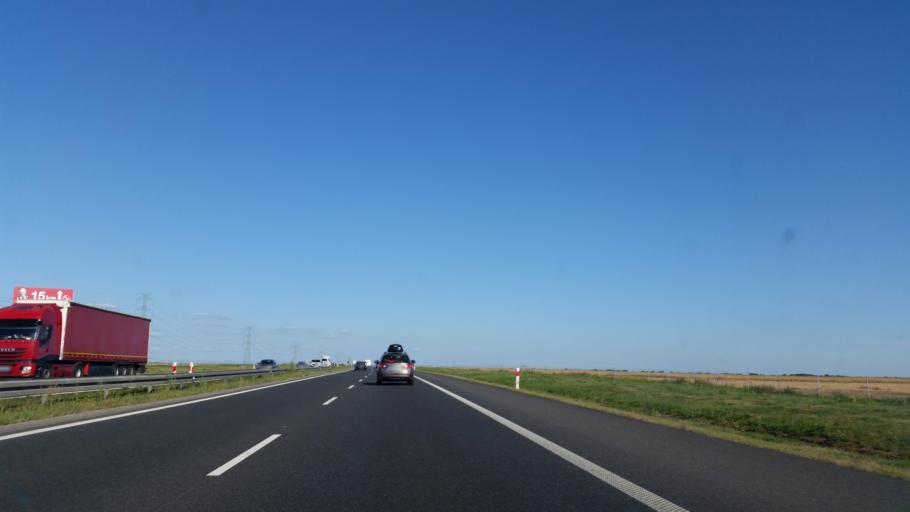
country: PL
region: Opole Voivodeship
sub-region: Powiat brzeski
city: Olszanka
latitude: 50.7374
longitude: 17.4755
